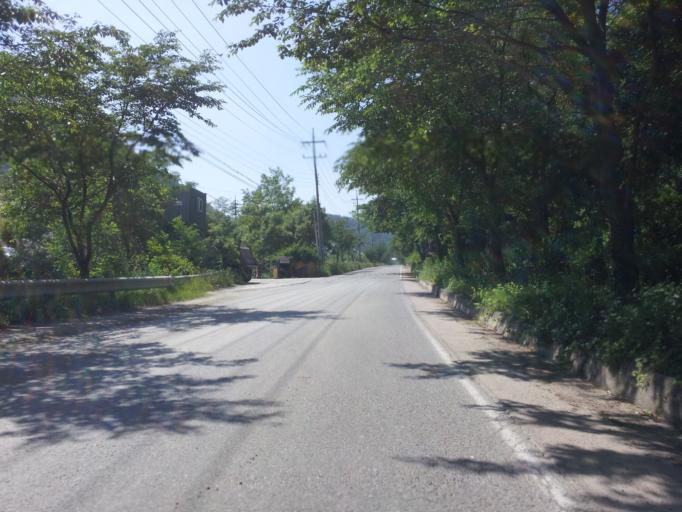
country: KR
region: Chungcheongbuk-do
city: Okcheon
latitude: 36.4524
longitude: 127.6775
